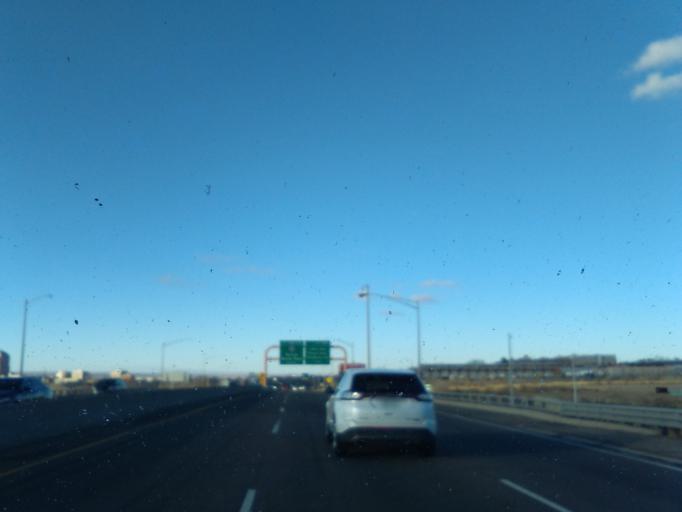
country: US
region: New Mexico
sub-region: Bernalillo County
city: Albuquerque
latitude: 35.0693
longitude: -106.6394
